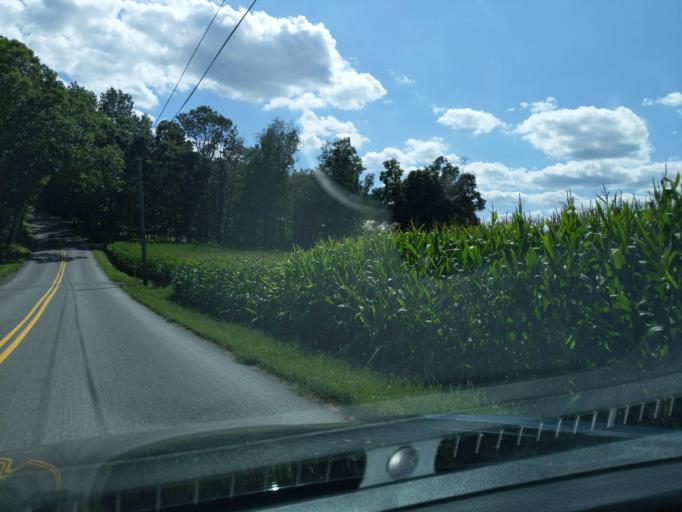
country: US
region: Pennsylvania
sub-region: Blair County
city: Tyrone
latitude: 40.6238
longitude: -78.2288
